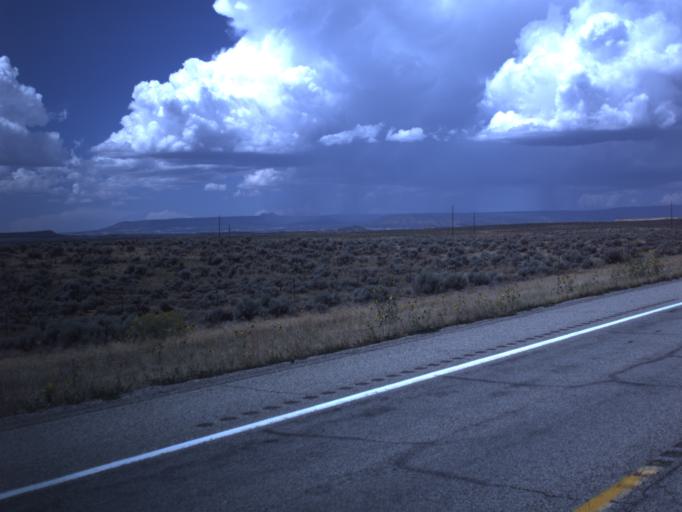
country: US
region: Utah
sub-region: San Juan County
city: Blanding
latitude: 37.5117
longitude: -109.4925
